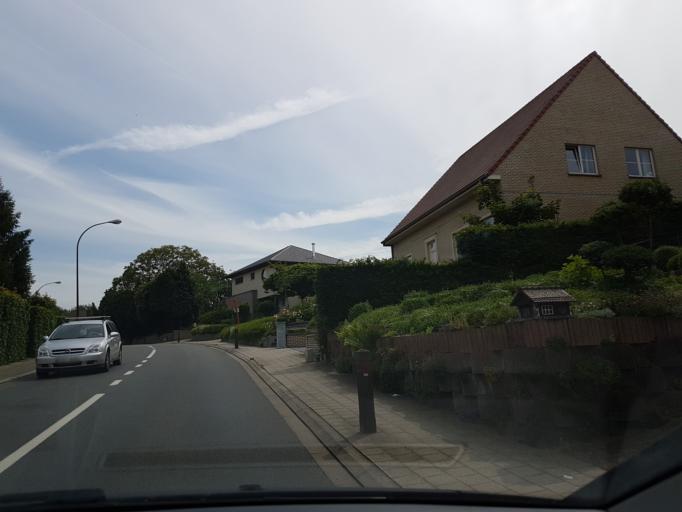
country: BE
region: Flanders
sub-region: Provincie Vlaams-Brabant
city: Asse
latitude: 50.9024
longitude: 4.2083
